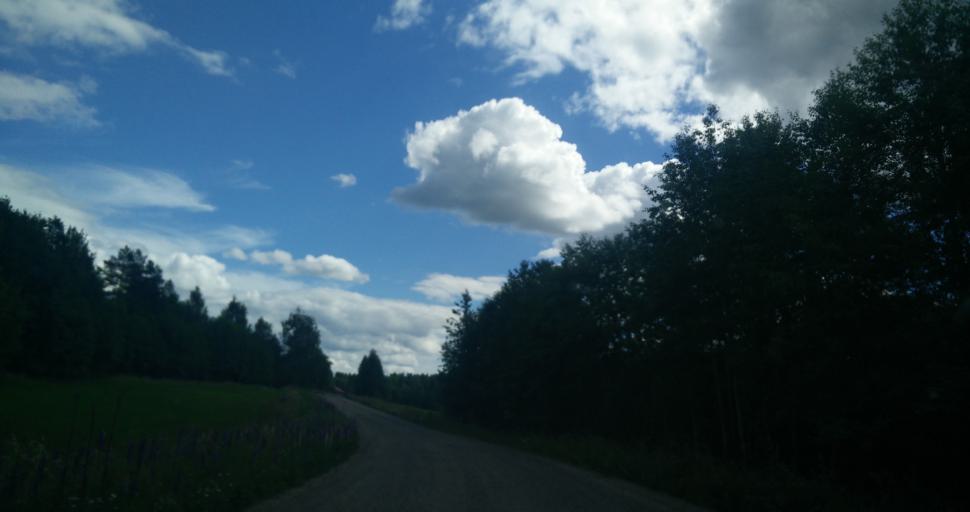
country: SE
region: Gaevleborg
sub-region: Nordanstigs Kommun
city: Bergsjoe
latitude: 62.0702
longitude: 16.7681
